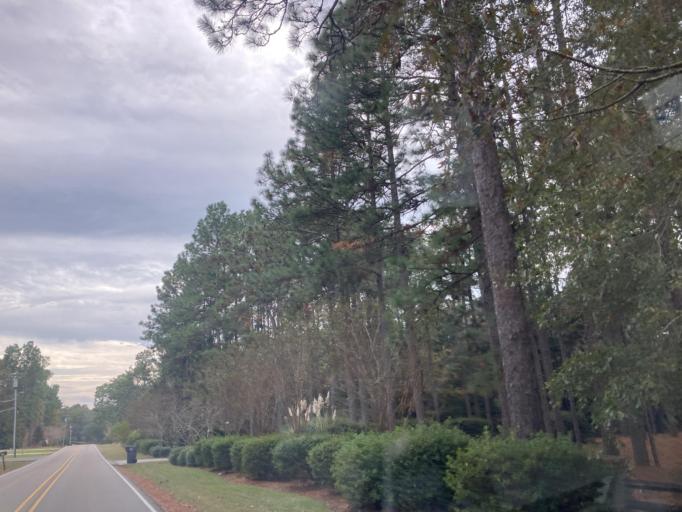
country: US
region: Mississippi
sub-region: Lamar County
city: West Hattiesburg
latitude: 31.3137
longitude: -89.4389
